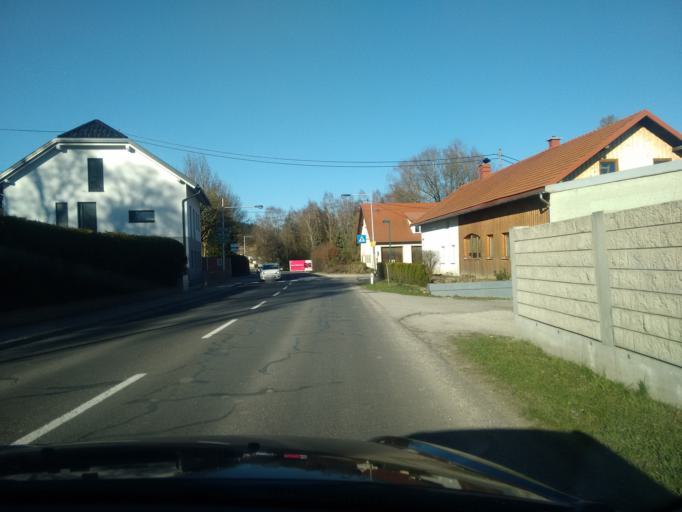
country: AT
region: Upper Austria
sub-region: Wels-Land
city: Offenhausen
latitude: 48.1554
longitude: 13.8370
